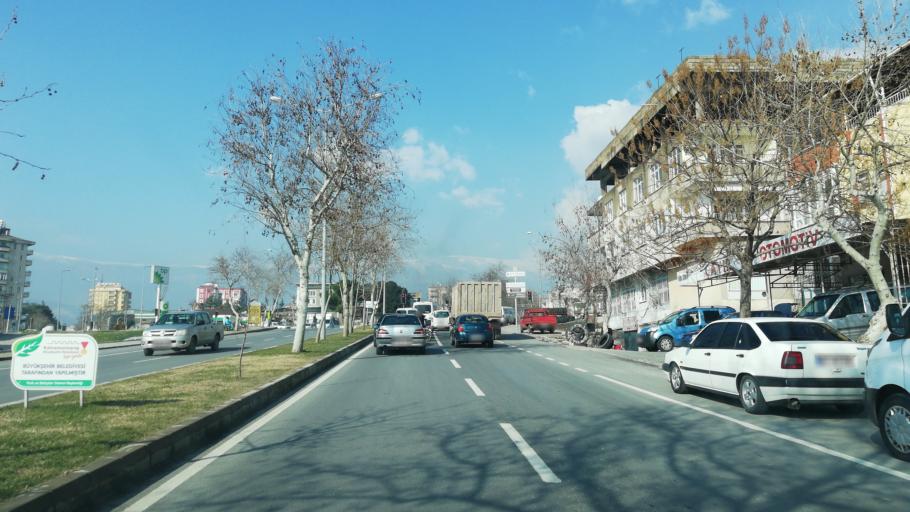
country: TR
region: Kahramanmaras
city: Kahramanmaras
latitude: 37.5703
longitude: 36.9428
